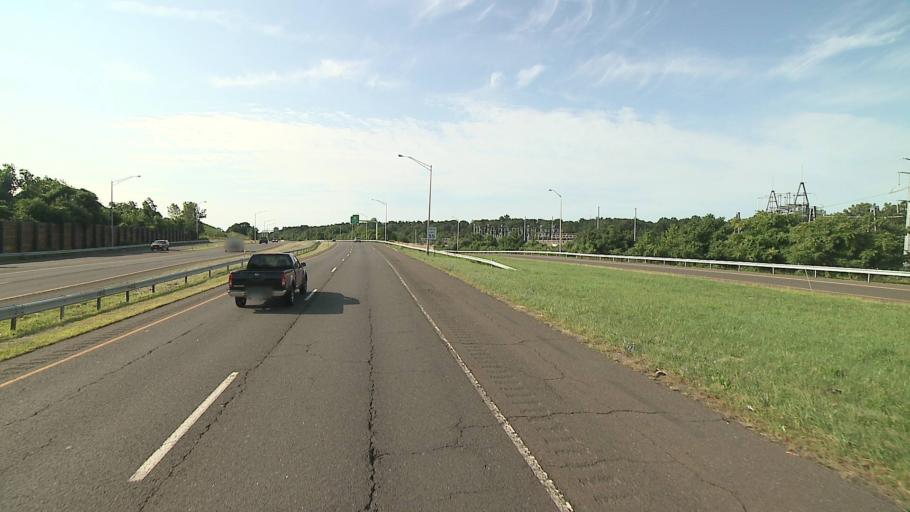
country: US
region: Connecticut
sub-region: Fairfield County
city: Norwalk
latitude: 41.1302
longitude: -73.4283
